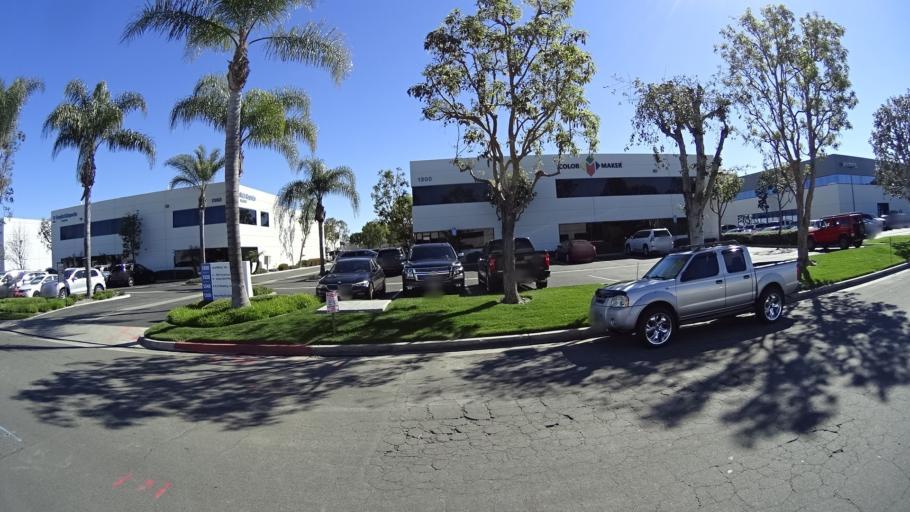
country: US
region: California
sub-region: Orange County
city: Yorba Linda
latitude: 33.8628
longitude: -117.8143
